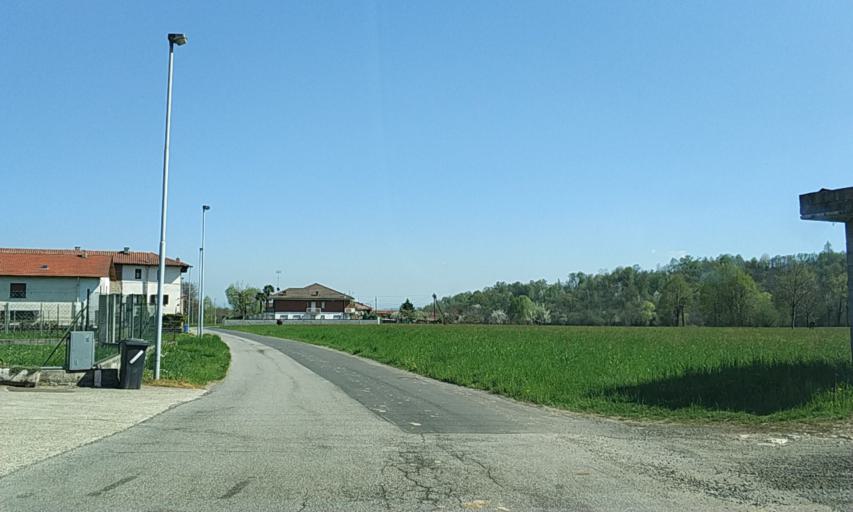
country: IT
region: Piedmont
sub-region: Provincia di Torino
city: Rivara
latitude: 45.3291
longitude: 7.6327
